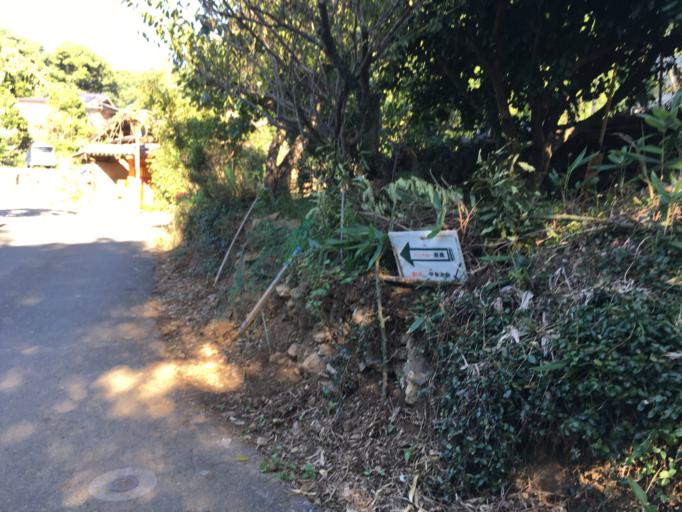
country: JP
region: Kumamoto
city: Kumamoto
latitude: 32.7987
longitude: 130.6573
